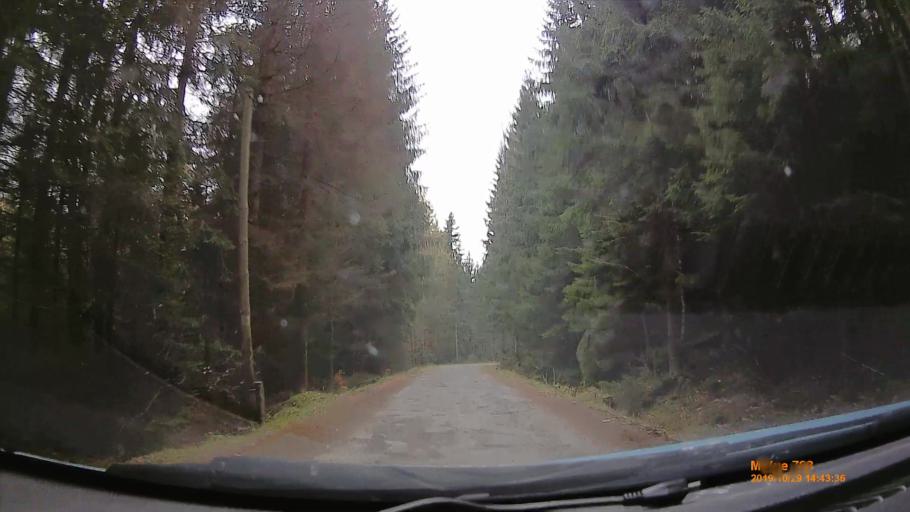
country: PL
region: Lower Silesian Voivodeship
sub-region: Powiat klodzki
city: Szczytna
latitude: 50.4475
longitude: 16.4214
